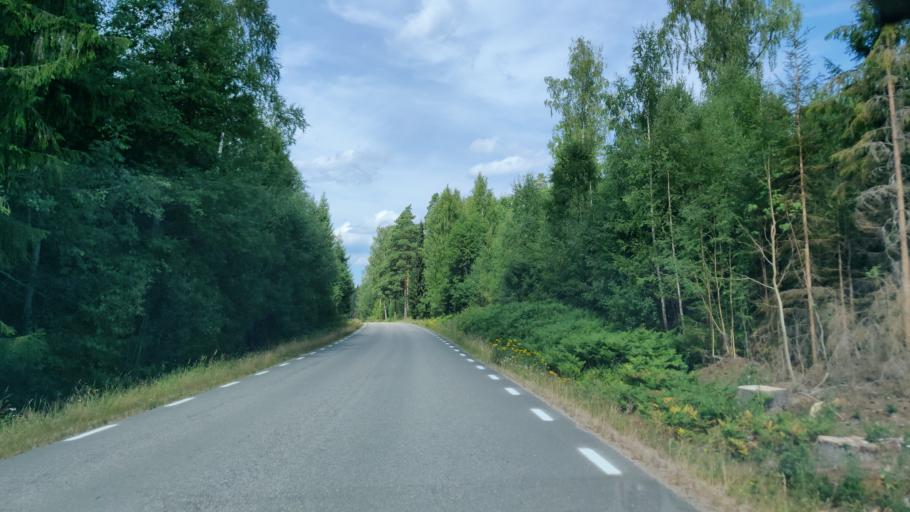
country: SE
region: Vaermland
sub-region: Hagfors Kommun
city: Ekshaerad
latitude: 60.0966
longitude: 13.5063
